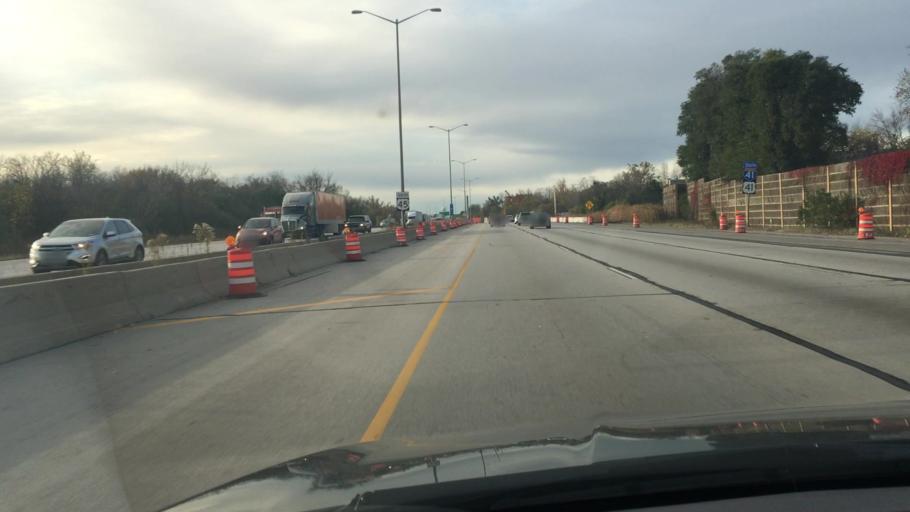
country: US
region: Wisconsin
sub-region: Waukesha County
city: Butler
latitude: 43.1012
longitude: -88.0584
